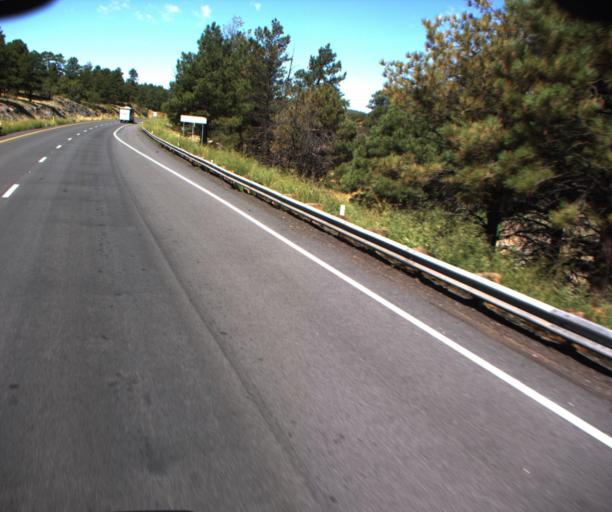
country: US
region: Arizona
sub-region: Coconino County
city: Williams
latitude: 35.2198
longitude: -112.2798
